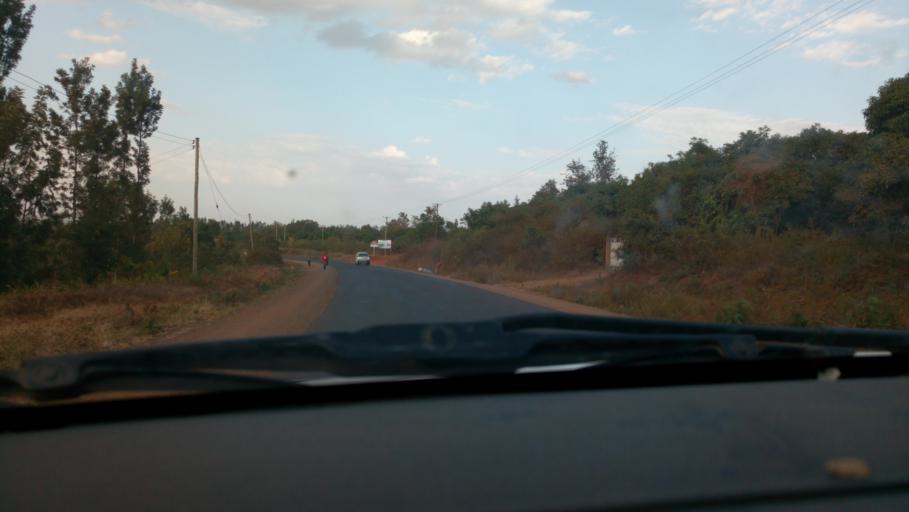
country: KE
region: Murang'a District
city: Maragua
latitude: -0.7860
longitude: 37.1387
